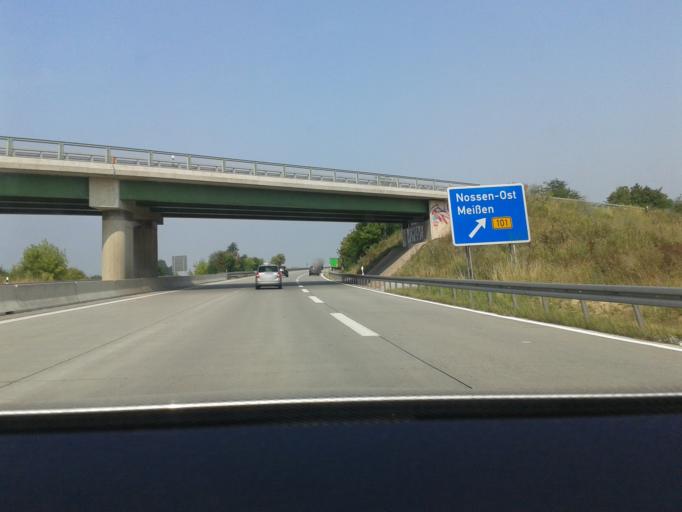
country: DE
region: Saxony
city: Nossen
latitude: 51.0567
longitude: 13.3449
